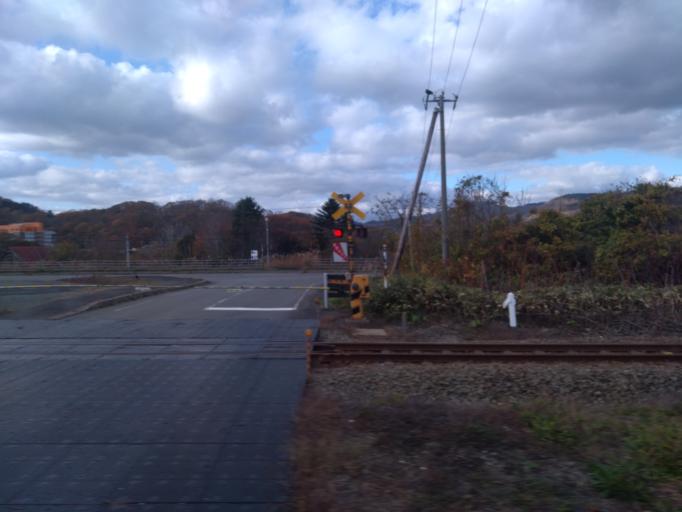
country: JP
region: Hokkaido
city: Niseko Town
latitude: 42.5866
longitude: 140.6412
